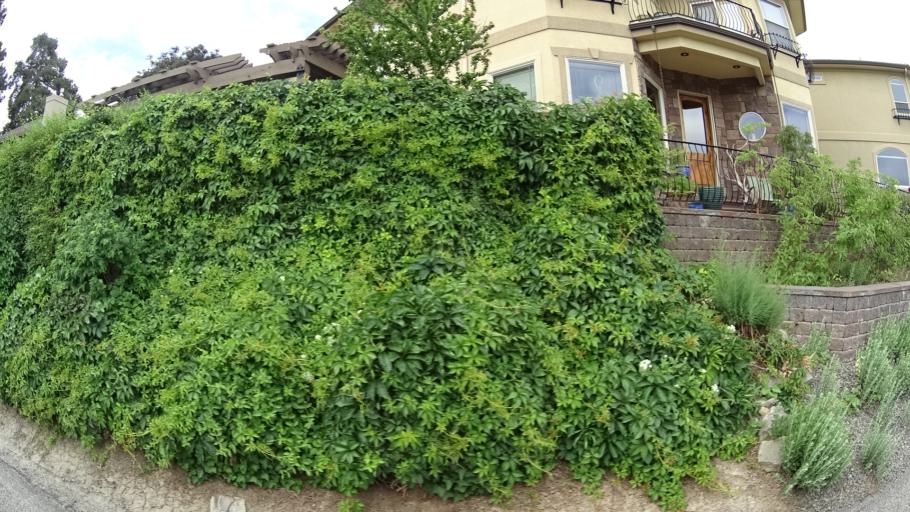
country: US
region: Idaho
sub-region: Ada County
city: Boise
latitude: 43.6036
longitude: -116.2161
